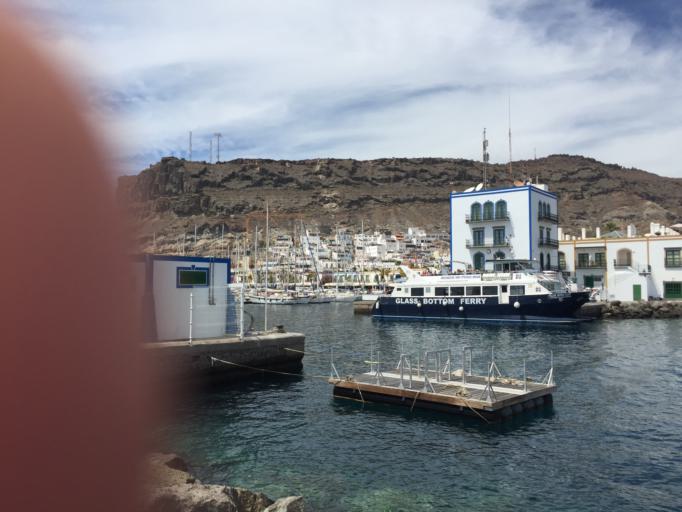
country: ES
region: Canary Islands
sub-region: Provincia de Las Palmas
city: Puerto Rico
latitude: 27.8158
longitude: -15.7638
